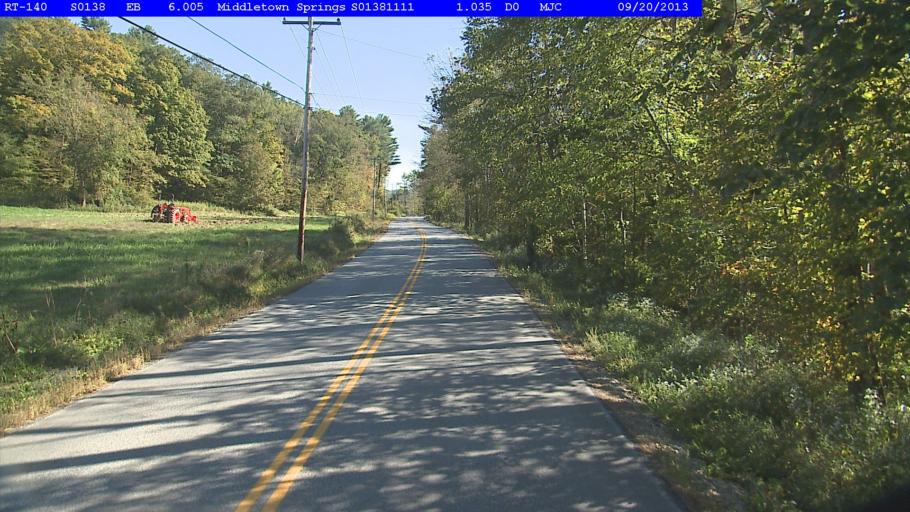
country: US
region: Vermont
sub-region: Rutland County
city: Poultney
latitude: 43.4920
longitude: -73.1547
